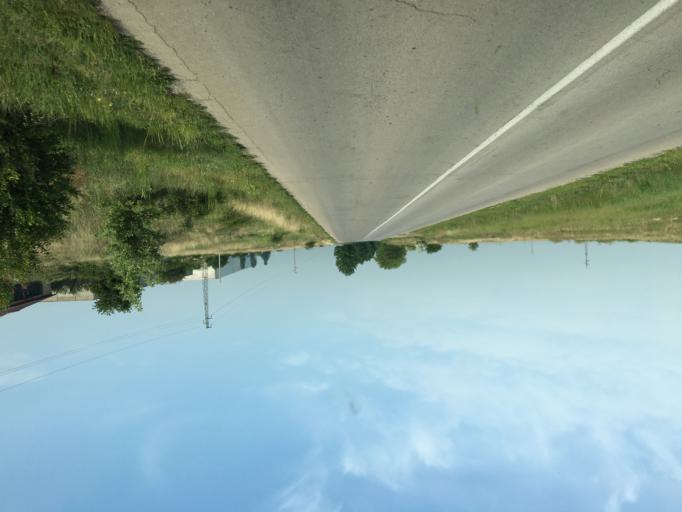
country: BG
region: Pernik
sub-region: Obshtina Radomir
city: Radomir
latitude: 42.4967
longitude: 23.0355
